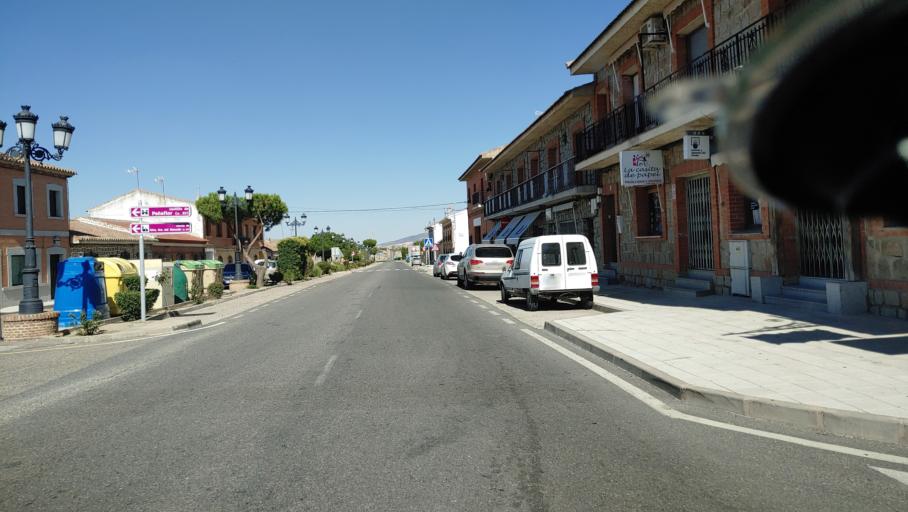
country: ES
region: Castille-La Mancha
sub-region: Province of Toledo
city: Cuerva
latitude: 39.6651
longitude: -4.2086
